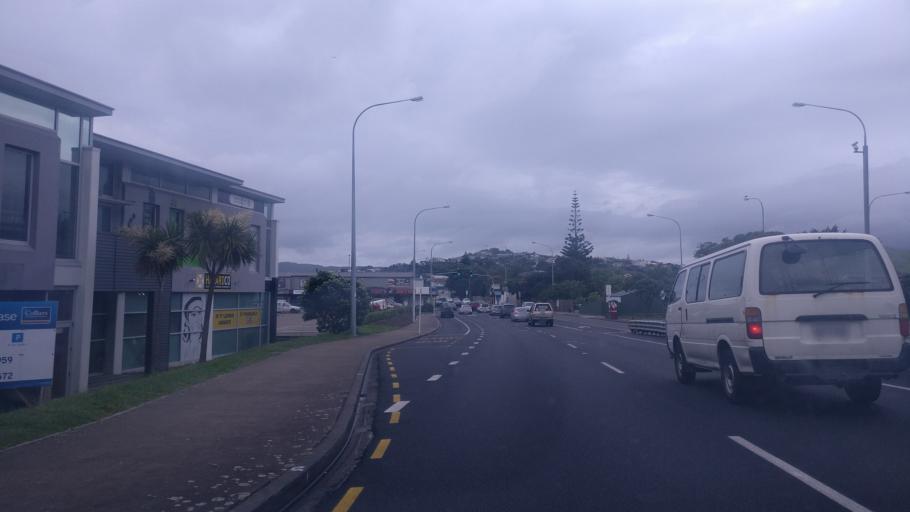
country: NZ
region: Wellington
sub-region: Porirua City
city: Porirua
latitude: -41.1022
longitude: 174.8699
